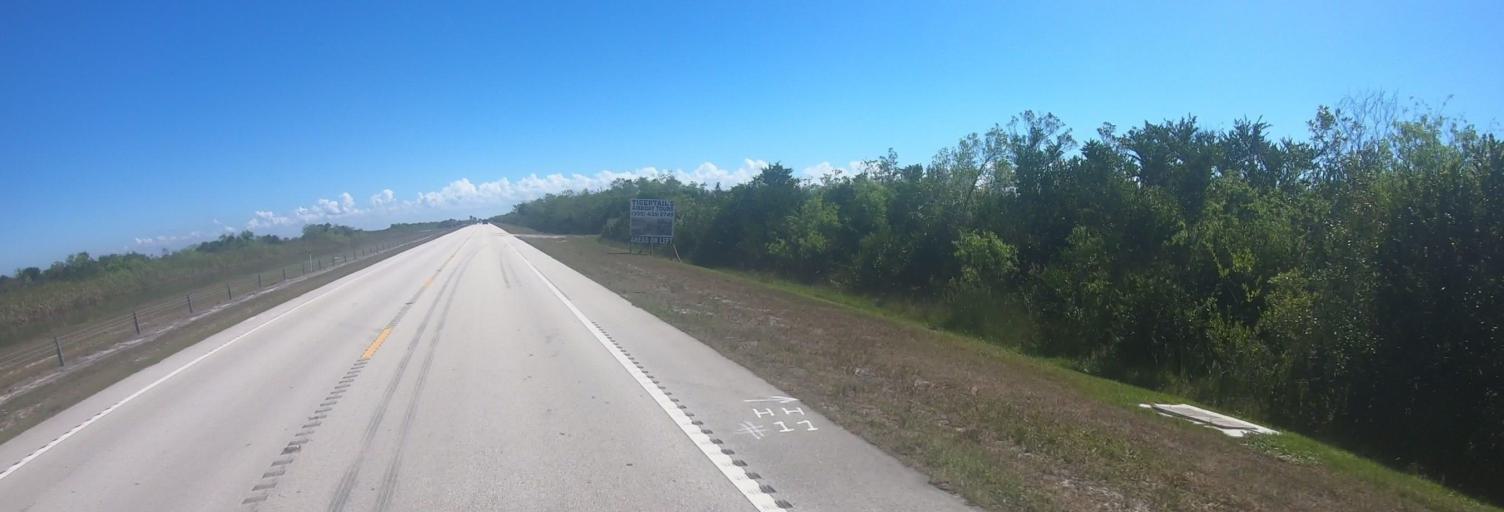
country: US
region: Florida
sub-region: Miami-Dade County
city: Kendall West
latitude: 25.7613
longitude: -80.7533
